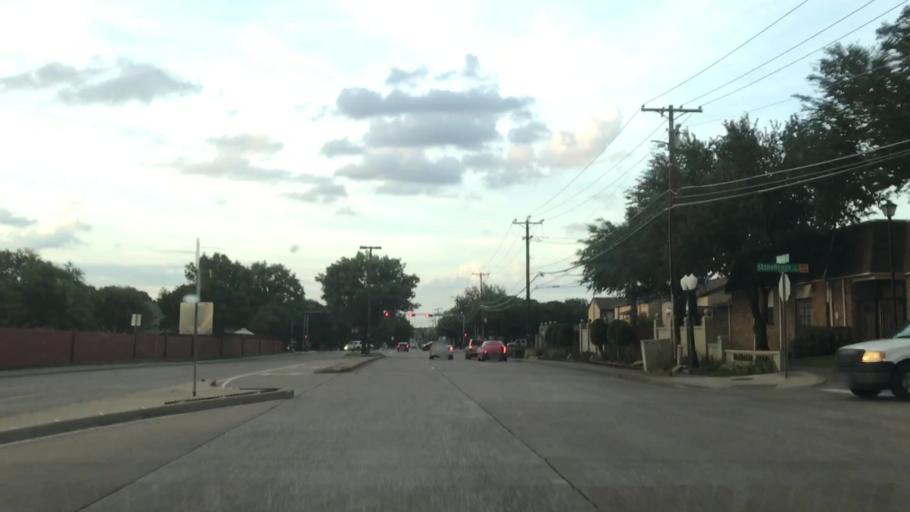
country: US
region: Texas
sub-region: Dallas County
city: Addison
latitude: 32.9590
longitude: -96.8537
